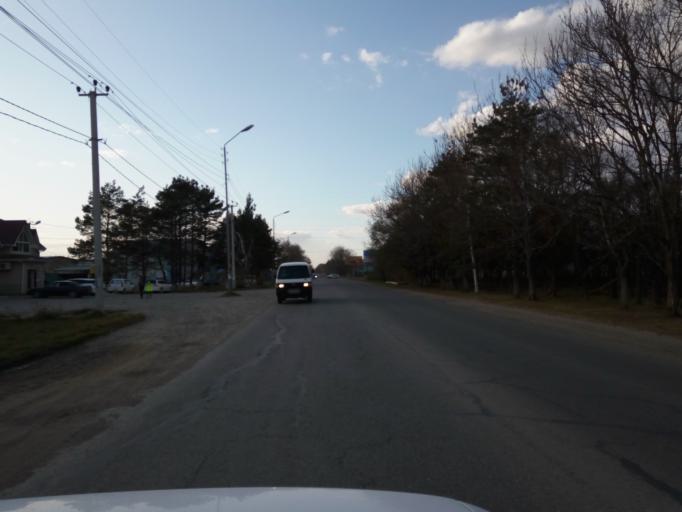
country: RU
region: Primorskiy
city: Dal'nerechensk
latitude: 45.9210
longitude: 133.7527
